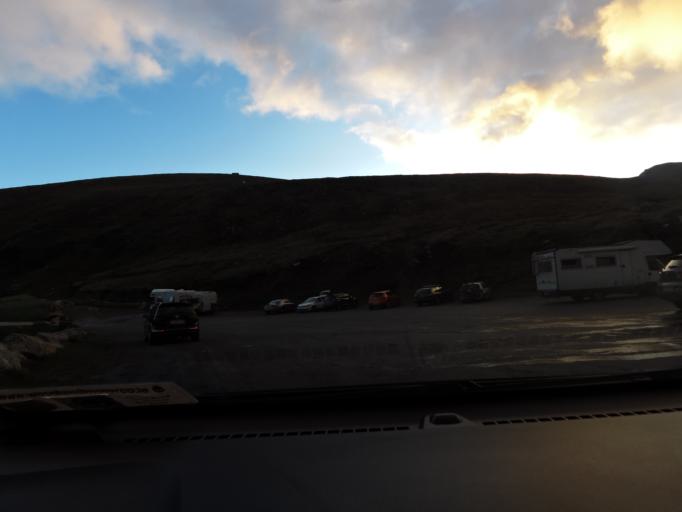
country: IE
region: Connaught
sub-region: Maigh Eo
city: Belmullet
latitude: 53.9675
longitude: -10.1954
